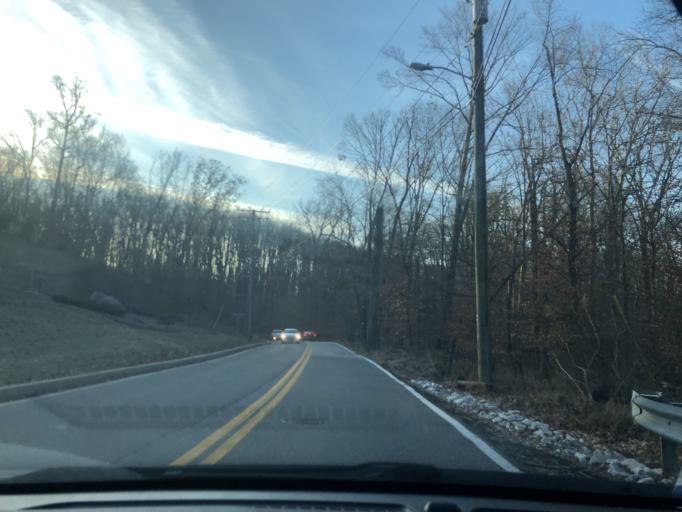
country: US
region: Maryland
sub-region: Howard County
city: Ilchester
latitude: 39.2637
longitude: -76.7660
